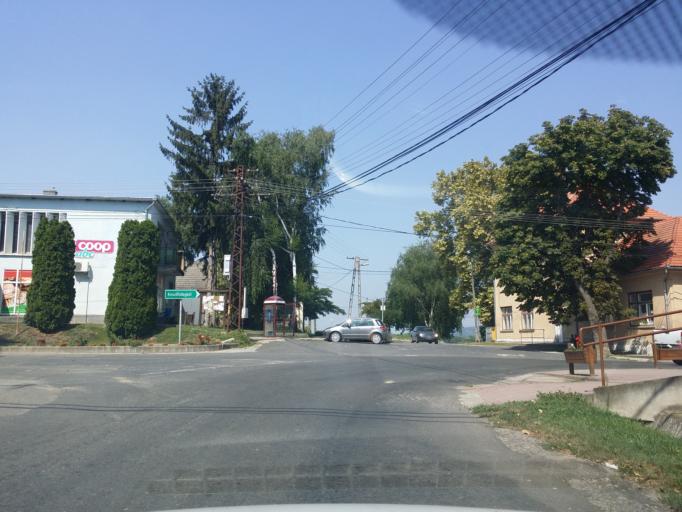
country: HU
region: Tolna
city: Hogyesz
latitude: 46.5783
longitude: 18.3907
